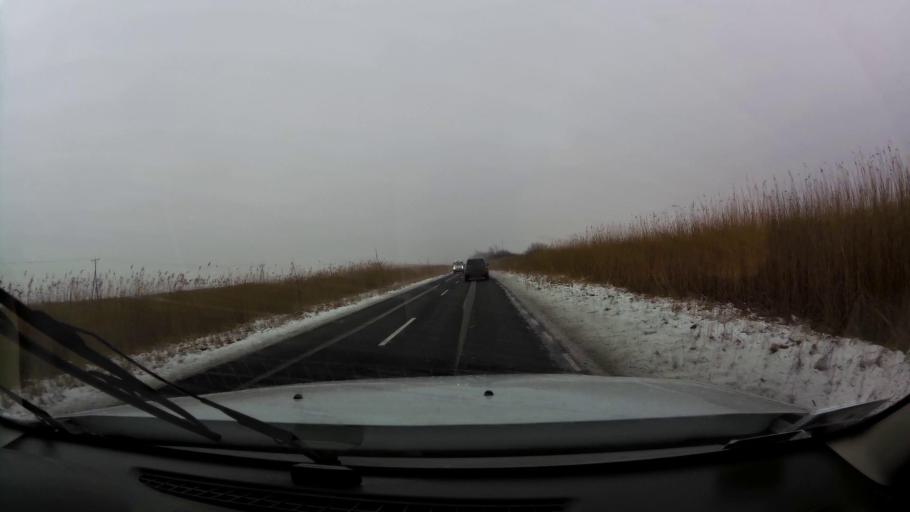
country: PL
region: West Pomeranian Voivodeship
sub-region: Powiat gryficki
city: Mrzezyno
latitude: 54.1302
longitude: 15.2780
